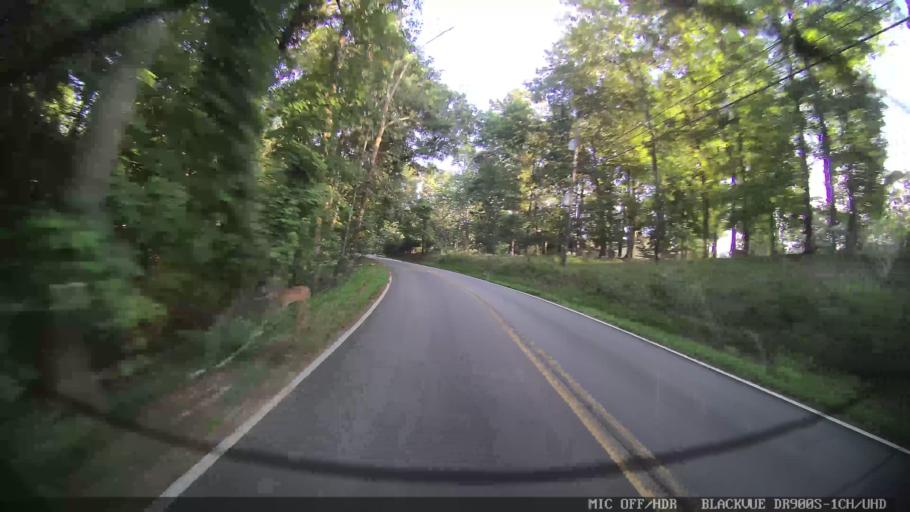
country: US
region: Georgia
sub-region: Bartow County
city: Emerson
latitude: 34.1803
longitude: -84.7063
